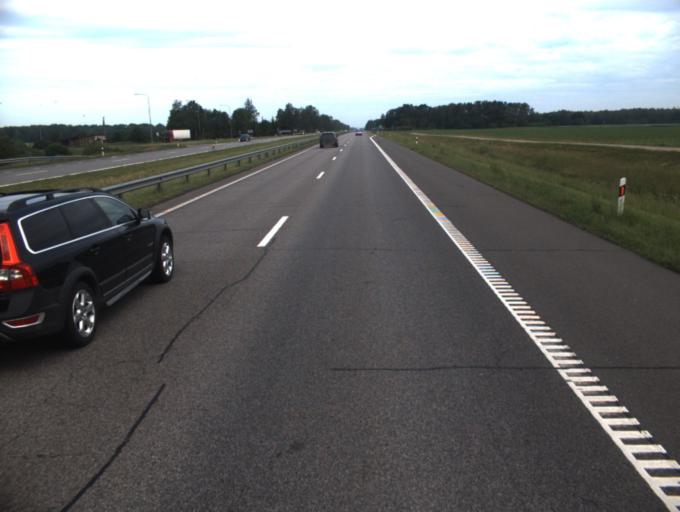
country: LT
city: Vilkija
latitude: 55.1223
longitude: 23.7534
